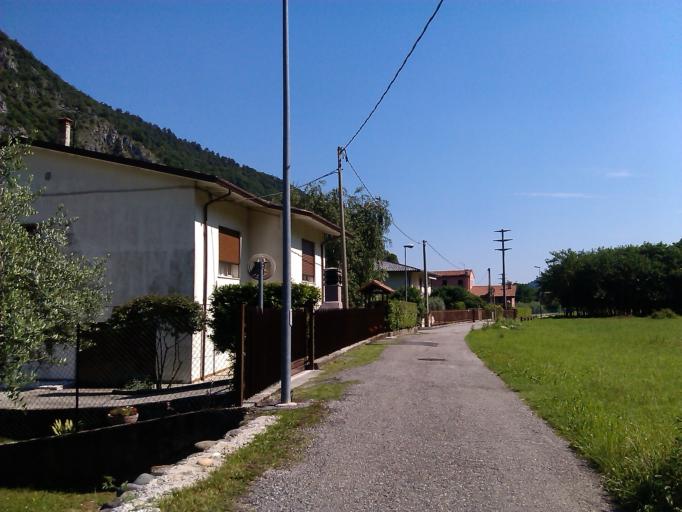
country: IT
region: Veneto
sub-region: Provincia di Vicenza
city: Solagna
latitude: 45.8128
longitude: 11.7163
